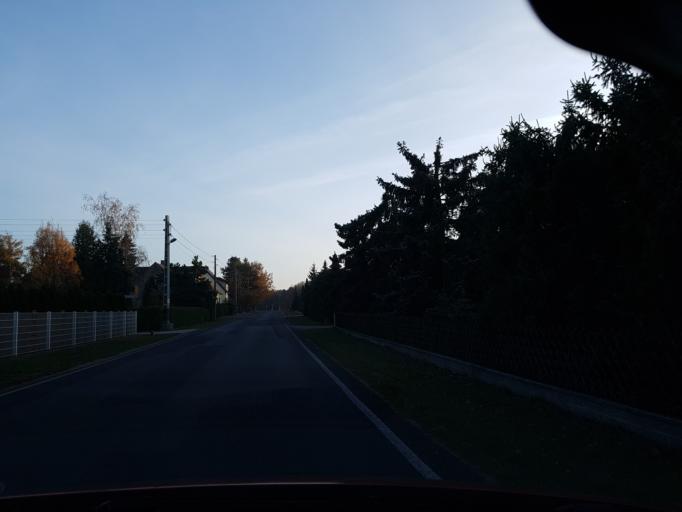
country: DE
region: Brandenburg
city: Bad Liebenwerda
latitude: 51.4803
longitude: 13.4210
